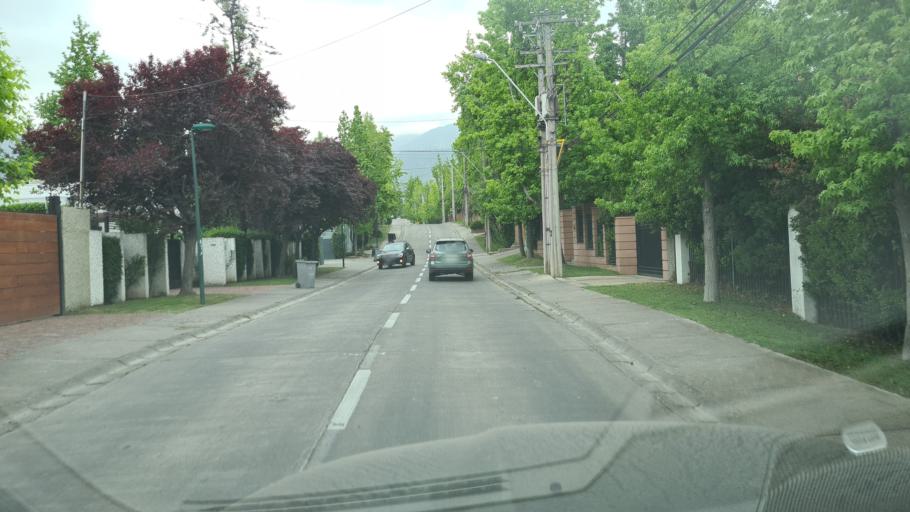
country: CL
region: Santiago Metropolitan
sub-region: Provincia de Santiago
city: Villa Presidente Frei, Nunoa, Santiago, Chile
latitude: -33.3414
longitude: -70.5071
